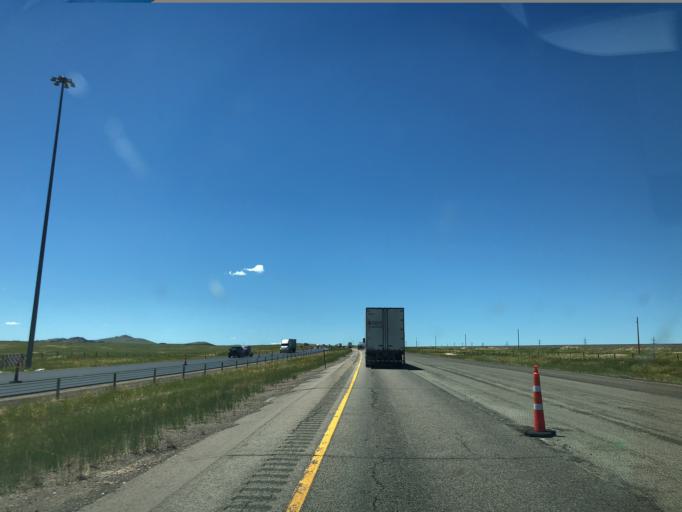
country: US
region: Wyoming
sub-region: Laramie County
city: Cheyenne
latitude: 41.0987
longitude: -105.1200
